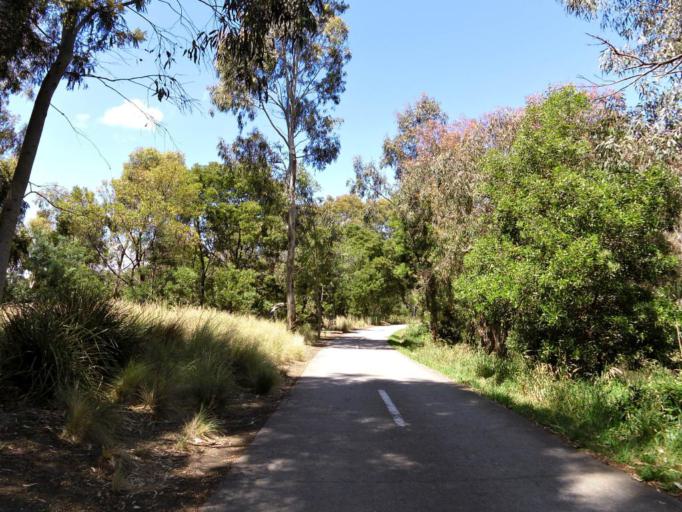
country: AU
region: Victoria
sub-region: Moreland
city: Coburg
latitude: -37.7505
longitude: 144.9811
